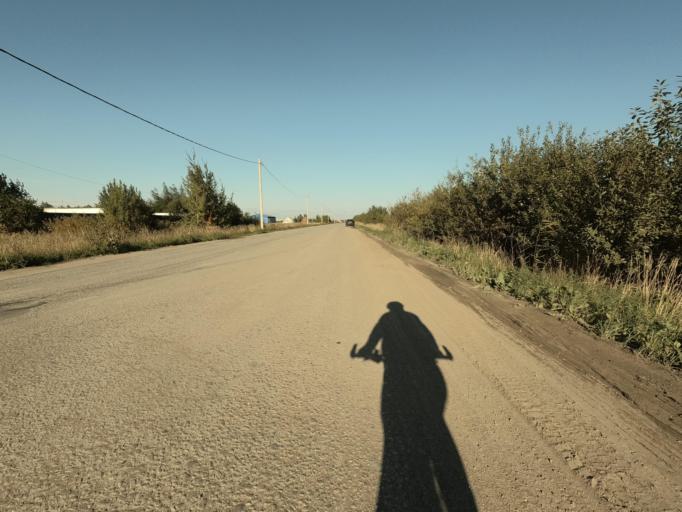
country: RU
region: St.-Petersburg
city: Petro-Slavyanka
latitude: 59.7651
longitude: 30.4861
